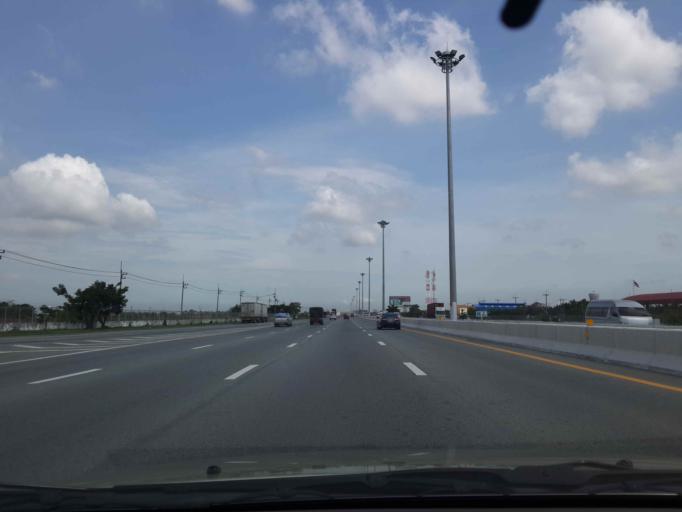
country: TH
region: Chachoengsao
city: Bang Pakong
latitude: 13.6017
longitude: 100.9501
